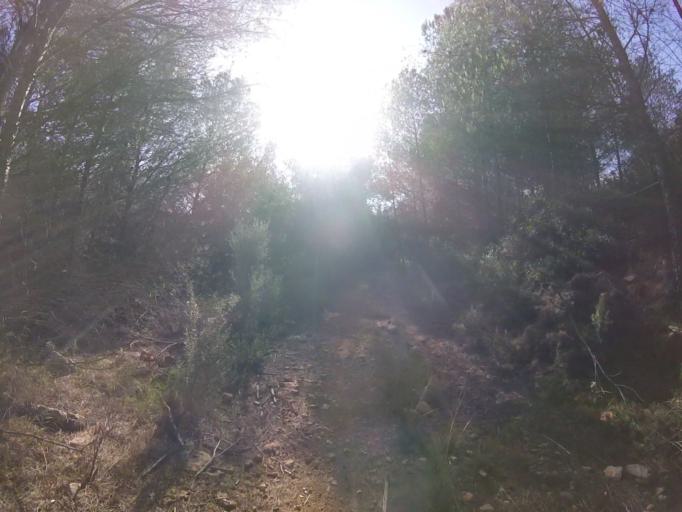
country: ES
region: Valencia
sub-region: Provincia de Castello
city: Alcoceber
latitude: 40.2929
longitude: 0.3212
